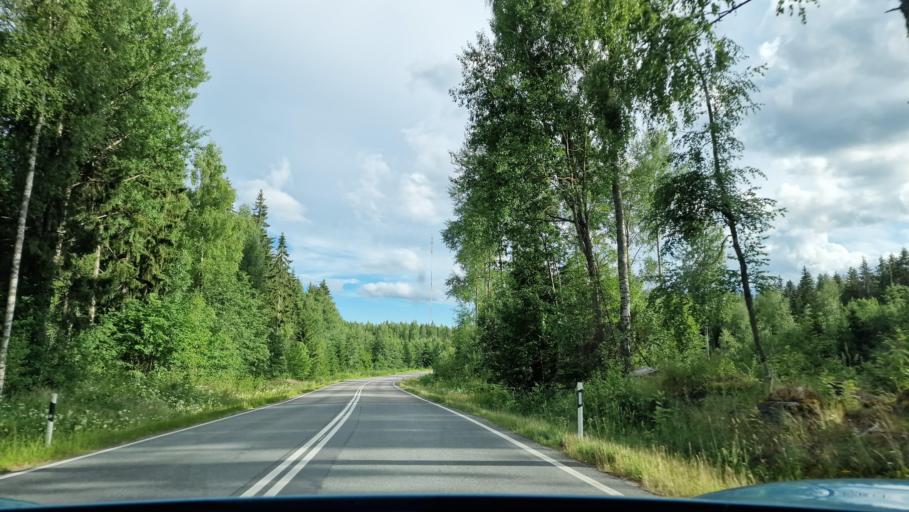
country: FI
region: Pirkanmaa
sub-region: Tampere
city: Paelkaene
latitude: 61.2570
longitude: 24.2293
